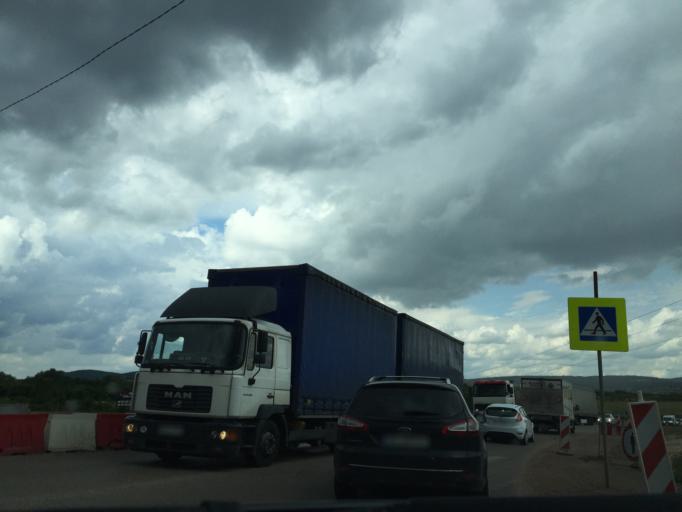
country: PL
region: Swietokrzyskie
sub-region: Powiat kielecki
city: Checiny
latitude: 50.7950
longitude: 20.4796
